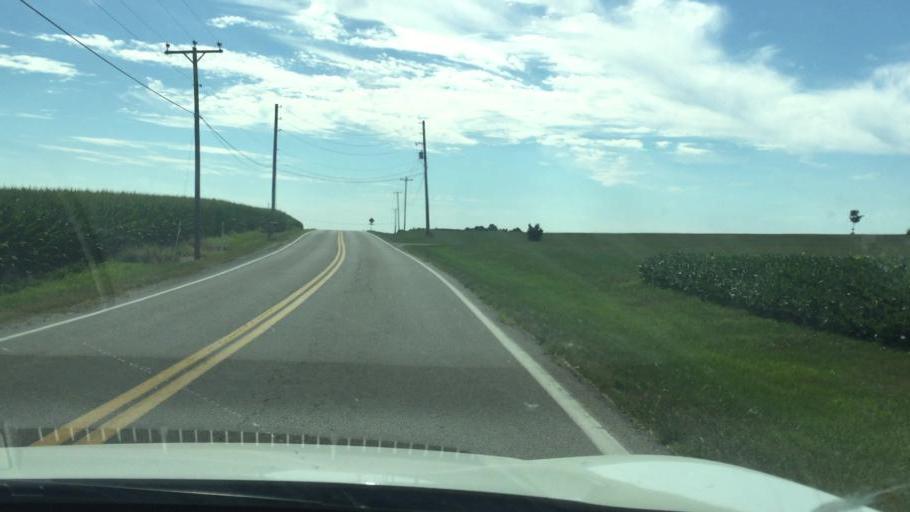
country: US
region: Ohio
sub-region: Clark County
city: Lisbon
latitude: 39.9420
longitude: -83.6431
